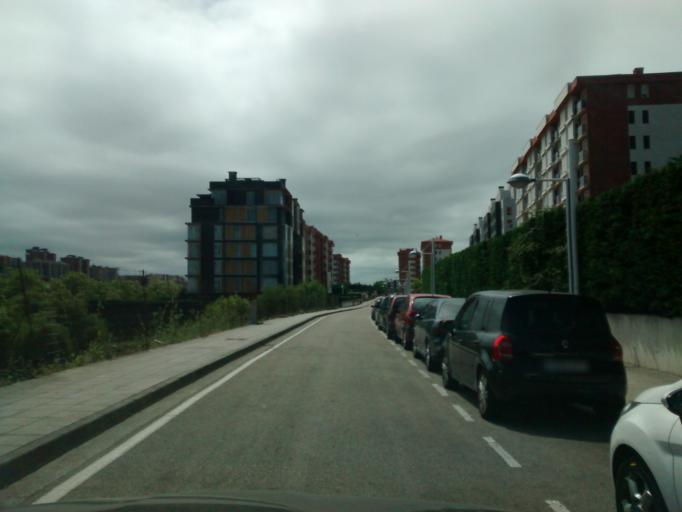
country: ES
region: Cantabria
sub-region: Provincia de Cantabria
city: Santander
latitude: 43.4733
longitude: -3.8104
